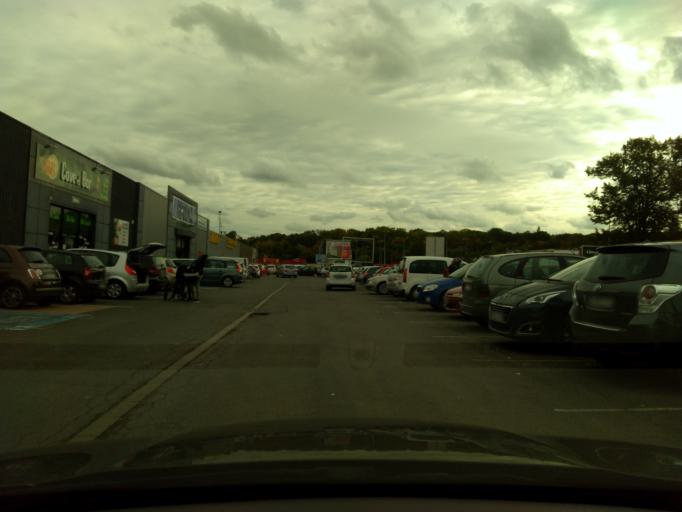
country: FR
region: Lorraine
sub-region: Departement de la Moselle
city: Augny
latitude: 49.0771
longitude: 6.1055
